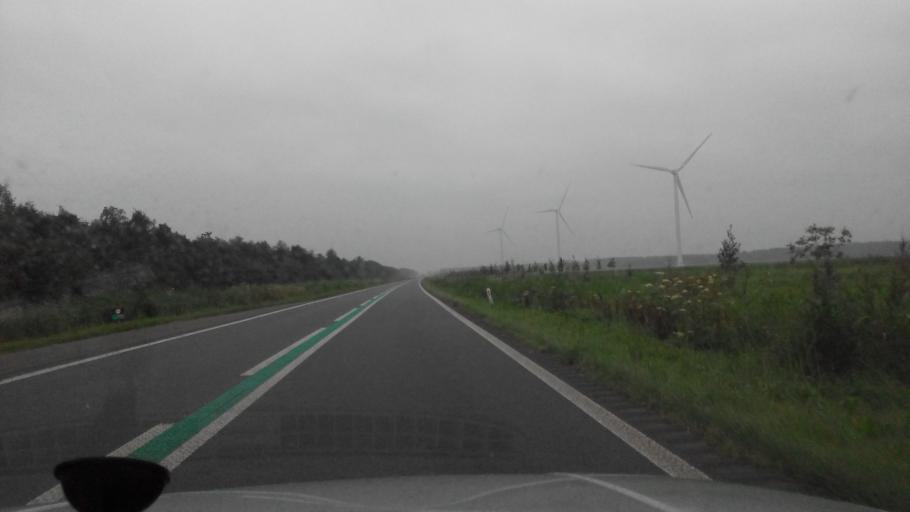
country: NL
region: Gelderland
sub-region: Gemeente Nijkerk
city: Nijkerk
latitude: 52.2974
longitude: 5.4542
